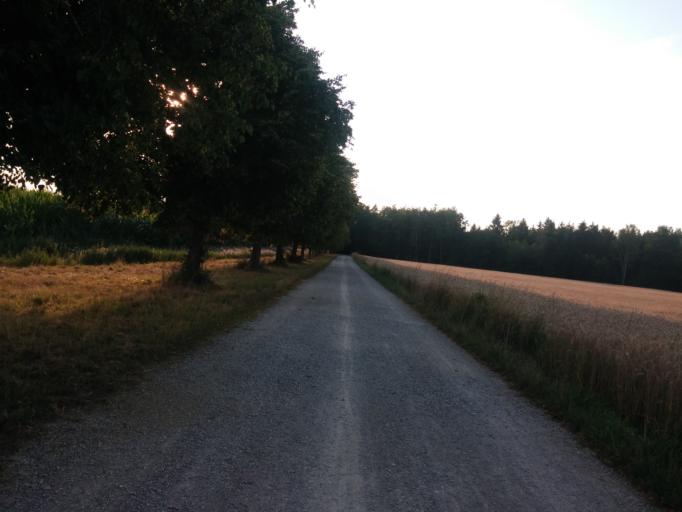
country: DE
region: Bavaria
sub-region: Upper Bavaria
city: Grasbrunn
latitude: 48.0623
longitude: 11.7637
